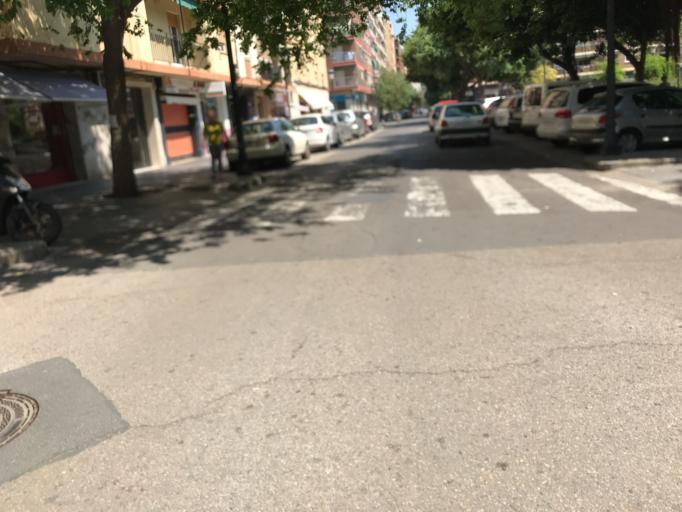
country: ES
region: Valencia
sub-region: Provincia de Valencia
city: Valencia
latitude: 39.4675
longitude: -0.3477
